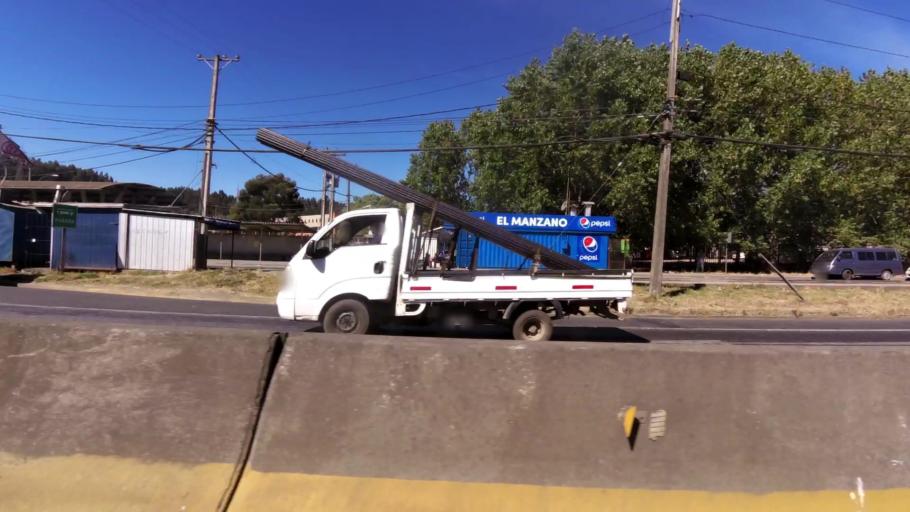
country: CL
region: Biobio
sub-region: Provincia de Concepcion
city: Concepcion
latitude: -36.8049
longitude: -73.0246
